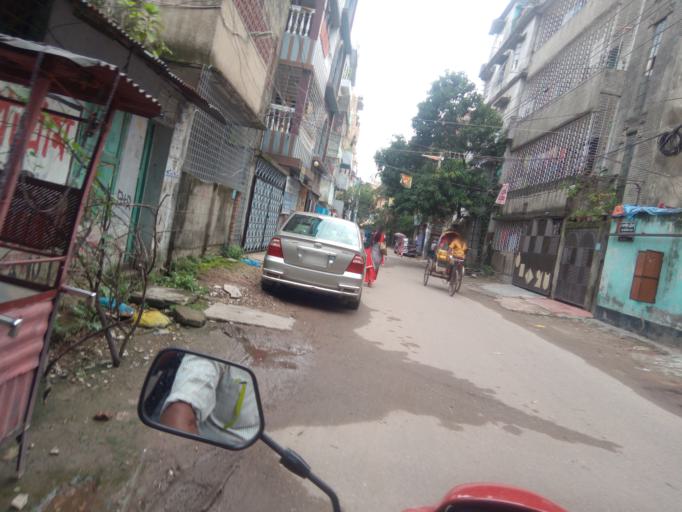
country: BD
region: Dhaka
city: Azimpur
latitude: 23.7634
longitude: 90.3606
